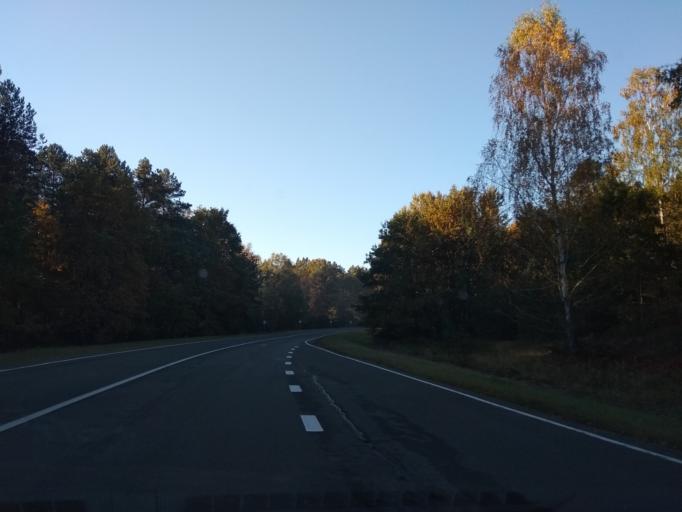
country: BY
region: Brest
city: Kobryn
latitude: 52.0341
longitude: 24.2701
